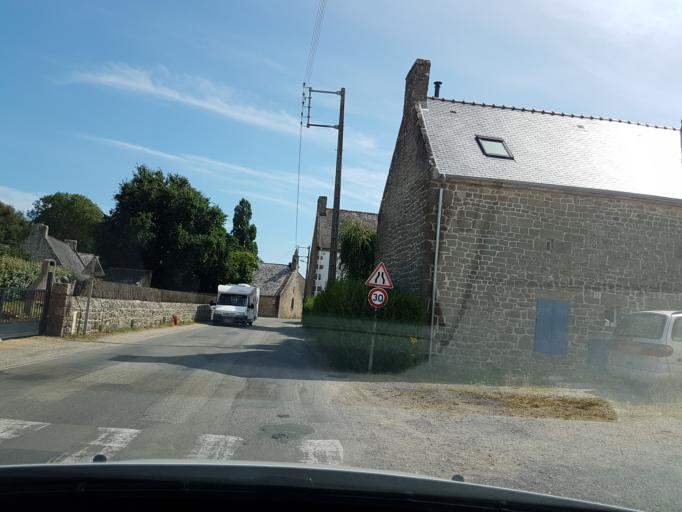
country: FR
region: Brittany
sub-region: Departement du Morbihan
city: Etel
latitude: 47.6710
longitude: -3.2210
